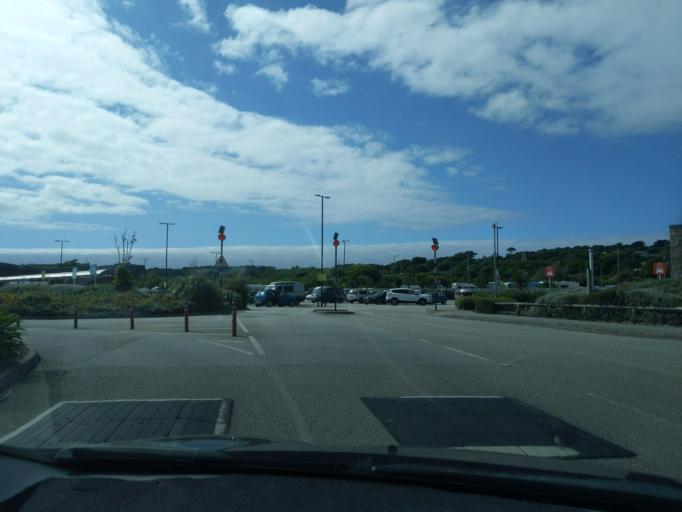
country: GB
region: England
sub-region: Cornwall
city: Penzance
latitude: 50.1283
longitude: -5.5168
